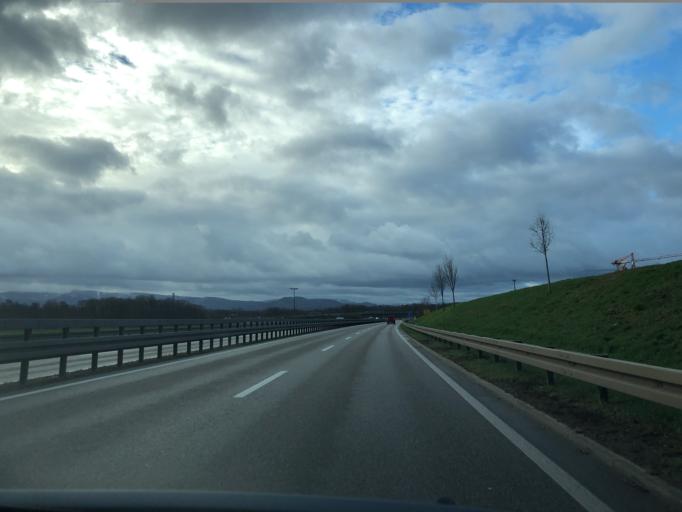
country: DE
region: Baden-Wuerttemberg
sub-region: Freiburg Region
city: Umkirch
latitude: 48.0333
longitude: 7.7787
